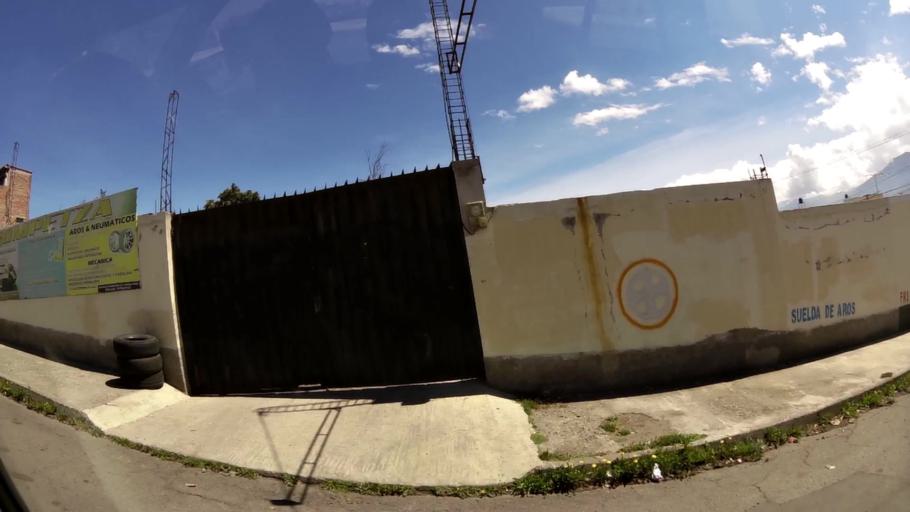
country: EC
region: Chimborazo
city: Riobamba
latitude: -1.6680
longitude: -78.6412
